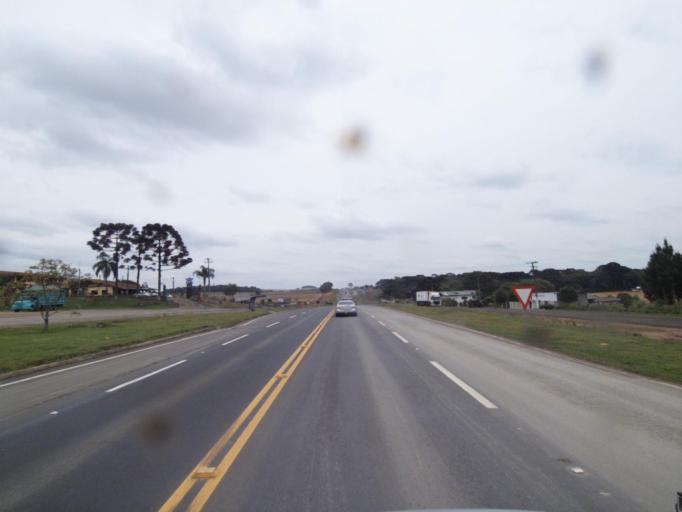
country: BR
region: Parana
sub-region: Irati
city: Irati
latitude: -25.4639
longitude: -50.5609
